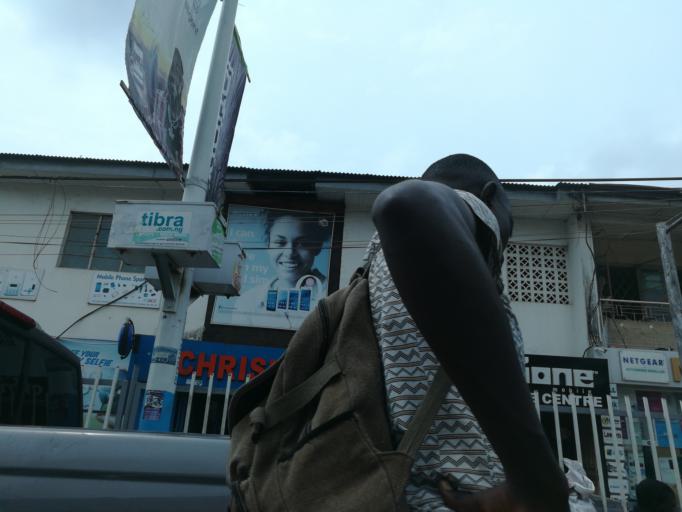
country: NG
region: Lagos
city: Ikeja
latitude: 6.5937
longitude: 3.3401
